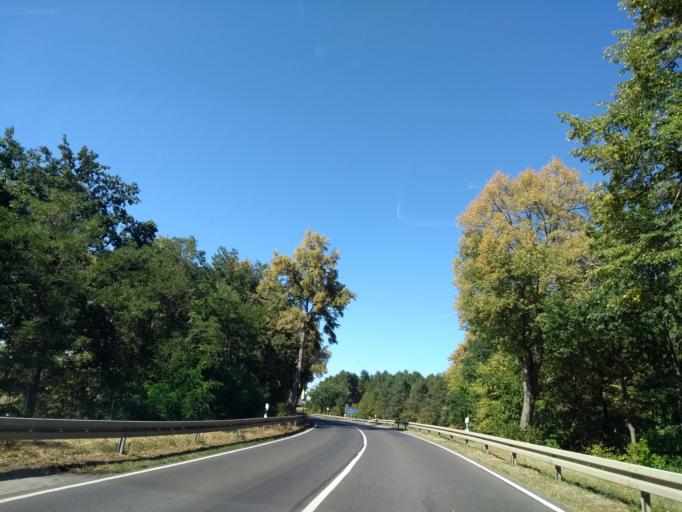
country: DE
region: Brandenburg
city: Lubbenau
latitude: 51.8337
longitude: 13.9762
